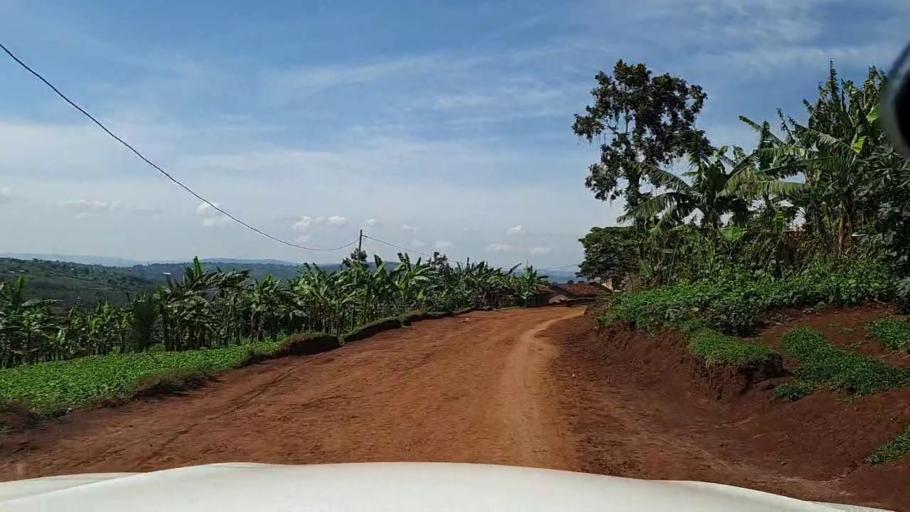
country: RW
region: Southern Province
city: Butare
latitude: -2.7046
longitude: 29.8451
